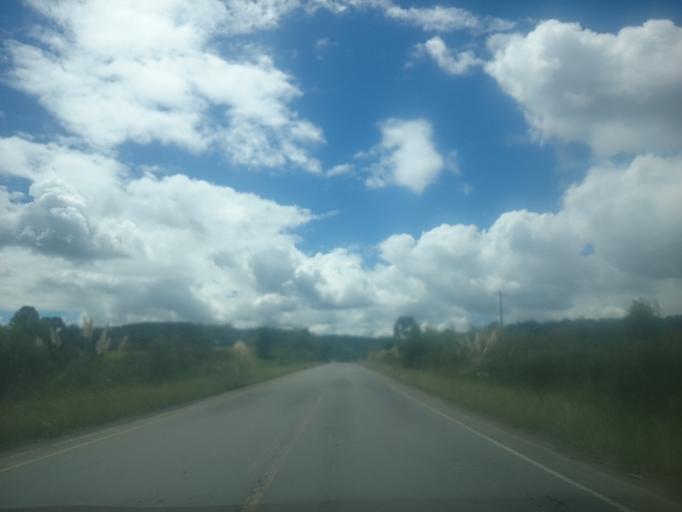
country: BR
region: Santa Catarina
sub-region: Correia Pinto
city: Correia Pinto
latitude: -27.6728
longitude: -50.2090
